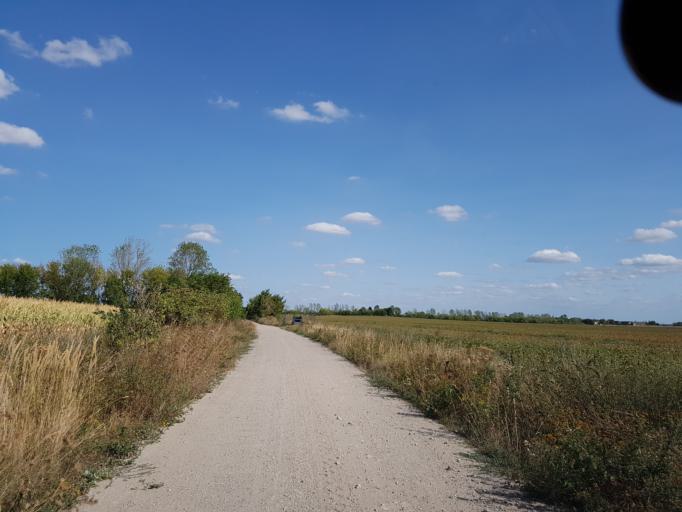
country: DE
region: Brandenburg
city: Treuenbrietzen
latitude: 52.0003
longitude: 12.8455
